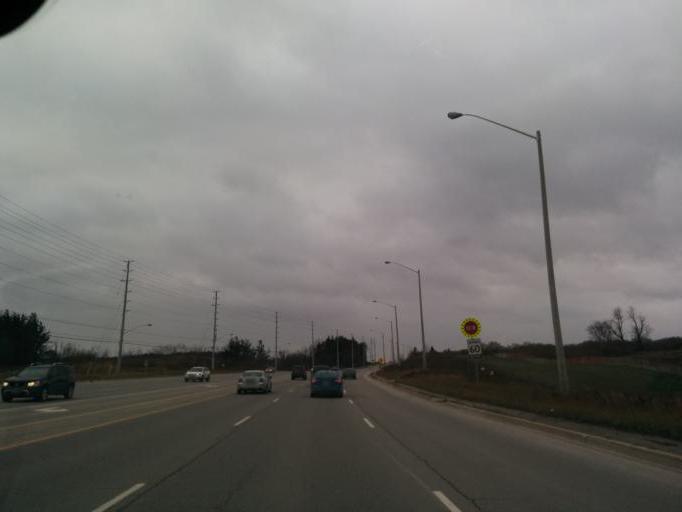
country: CA
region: Ontario
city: Brampton
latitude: 43.7524
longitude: -79.8039
